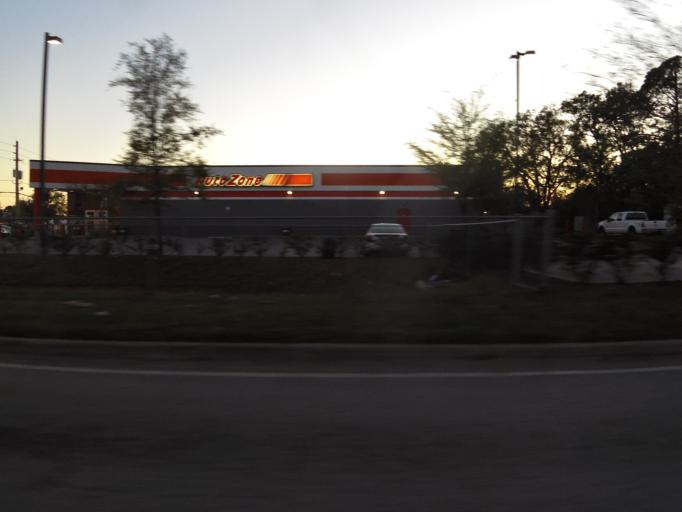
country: US
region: Florida
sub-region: Duval County
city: Jacksonville
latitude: 30.2641
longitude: -81.6225
